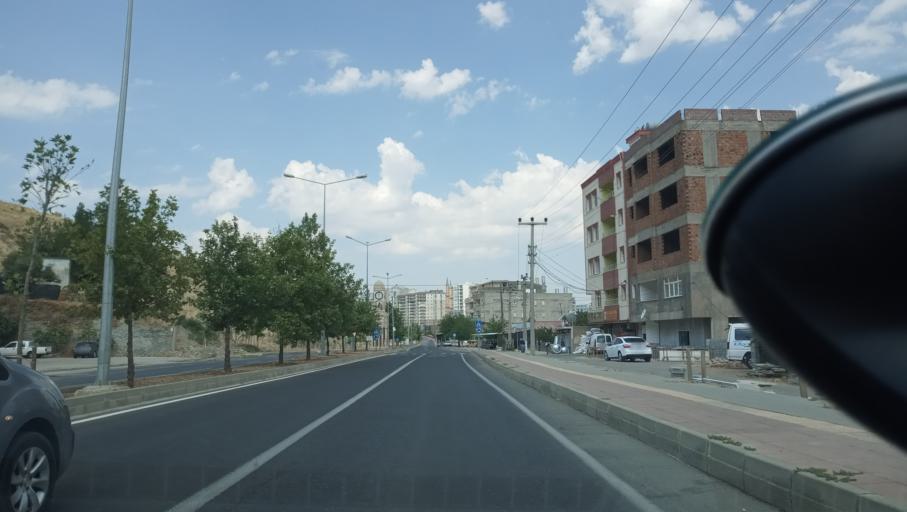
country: TR
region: Mardin
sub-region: Mardin Ilcesi
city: Mardin
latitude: 37.3223
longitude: 40.7385
